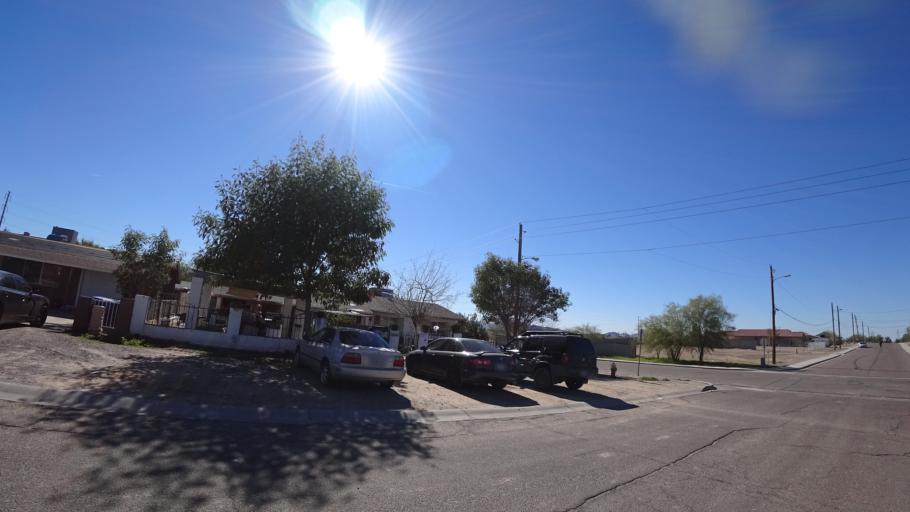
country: US
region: Arizona
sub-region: Maricopa County
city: Avondale
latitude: 33.4134
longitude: -112.3317
